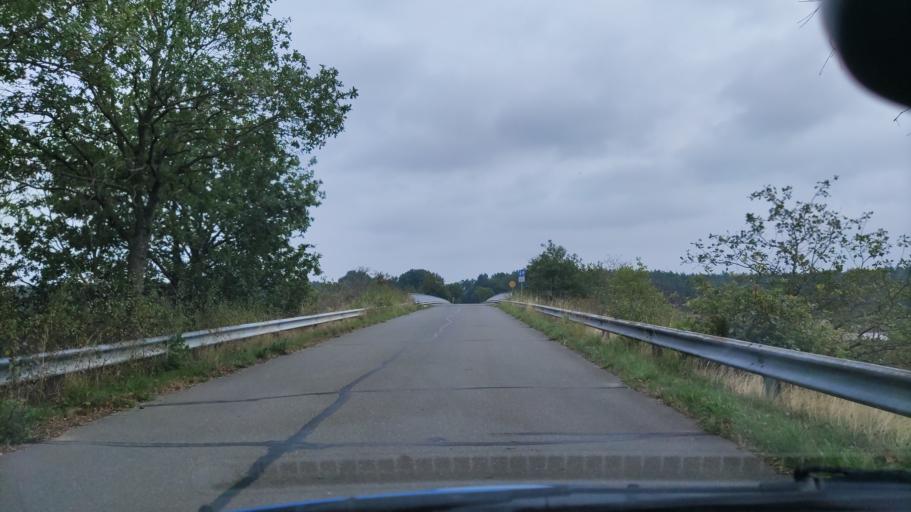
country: DE
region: Lower Saxony
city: Vastorf
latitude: 53.1515
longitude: 10.5496
